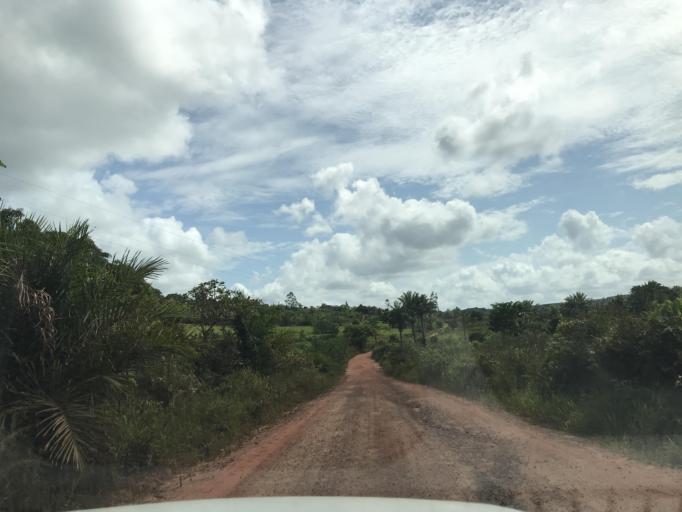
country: BR
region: Bahia
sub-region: Entre Rios
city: Entre Rios
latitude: -12.1684
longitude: -38.0918
